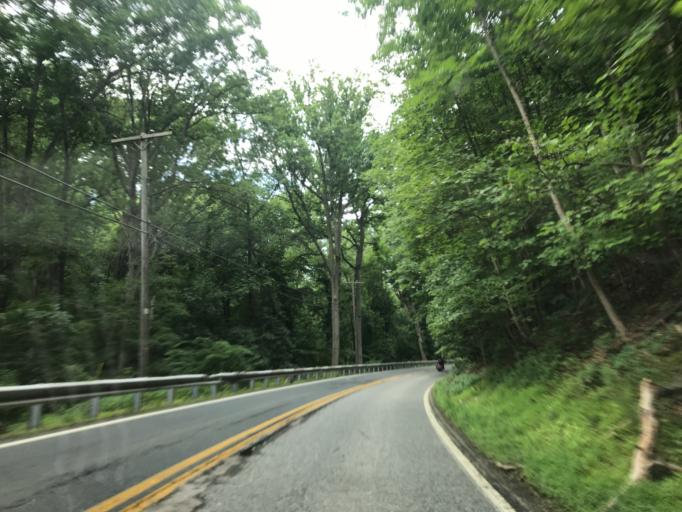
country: US
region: Maryland
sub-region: Harford County
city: Bel Air North
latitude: 39.6126
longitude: -76.4007
